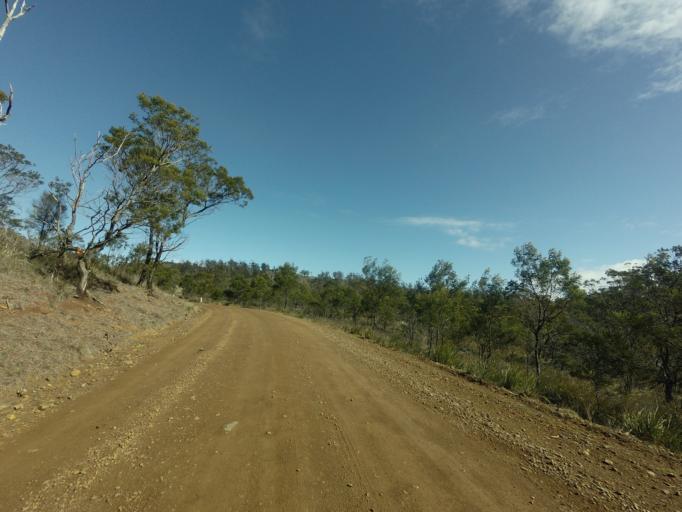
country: AU
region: Tasmania
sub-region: Sorell
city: Sorell
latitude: -42.4063
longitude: 147.9551
